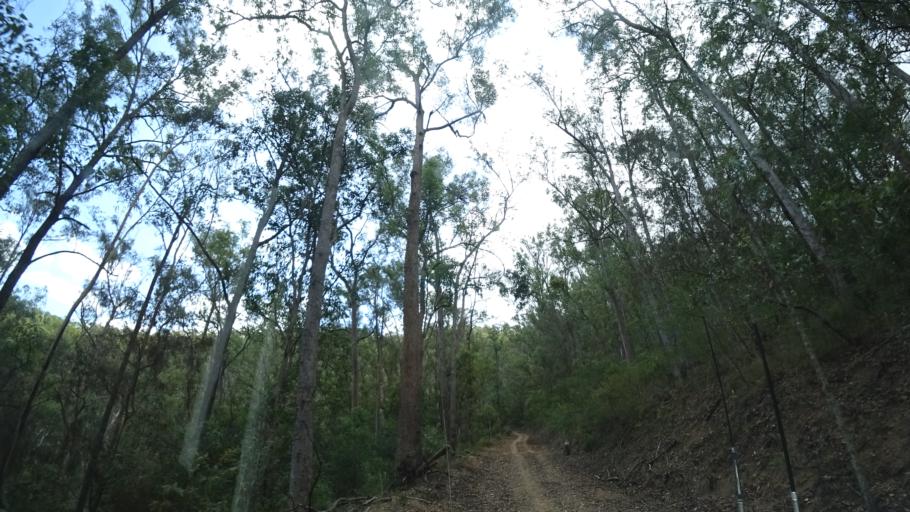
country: AU
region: Queensland
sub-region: Moreton Bay
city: Highvale
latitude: -27.3672
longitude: 152.7352
